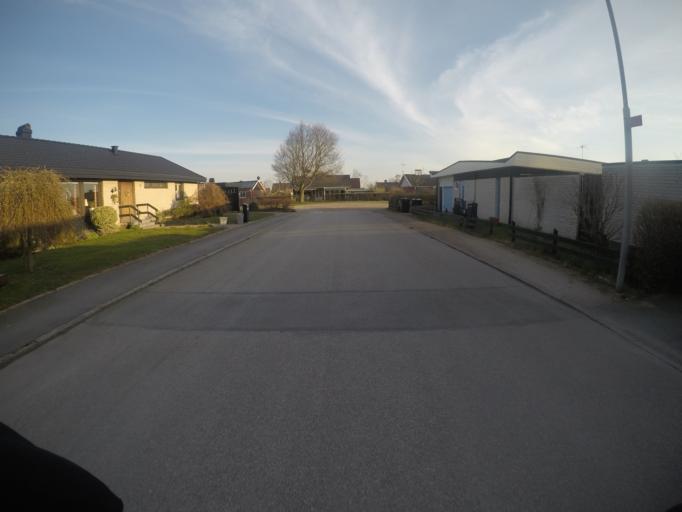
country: SE
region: Halland
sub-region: Laholms Kommun
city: Laholm
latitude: 56.5034
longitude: 13.0290
